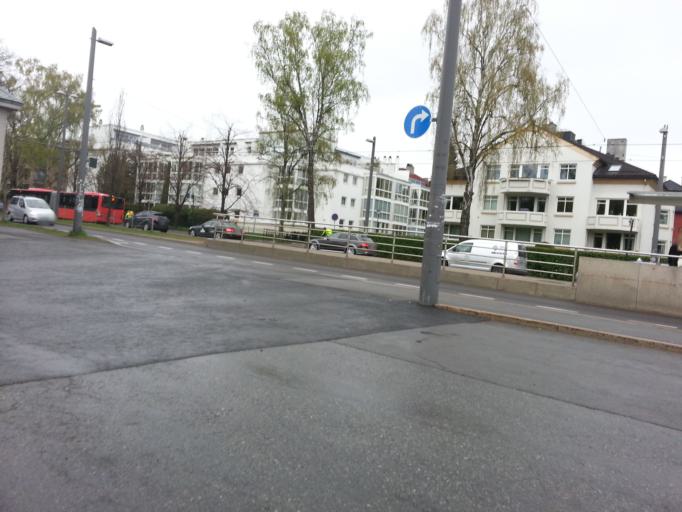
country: NO
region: Oslo
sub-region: Oslo
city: Sjolyststranda
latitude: 59.9249
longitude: 10.7082
